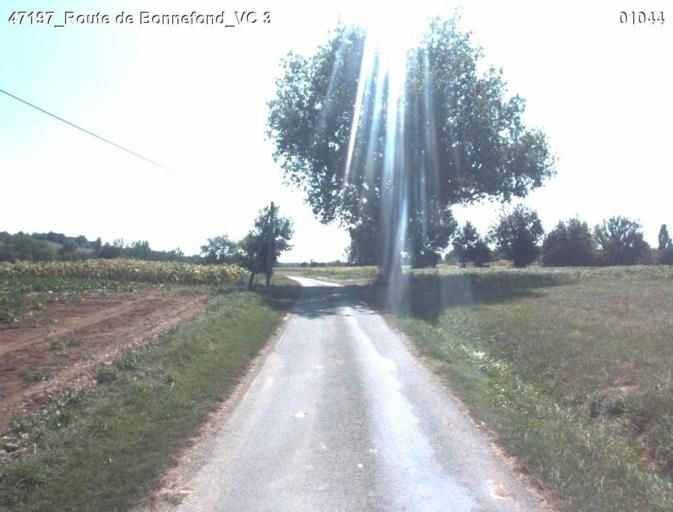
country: FR
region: Aquitaine
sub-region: Departement du Lot-et-Garonne
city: Laplume
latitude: 44.1046
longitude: 0.4753
